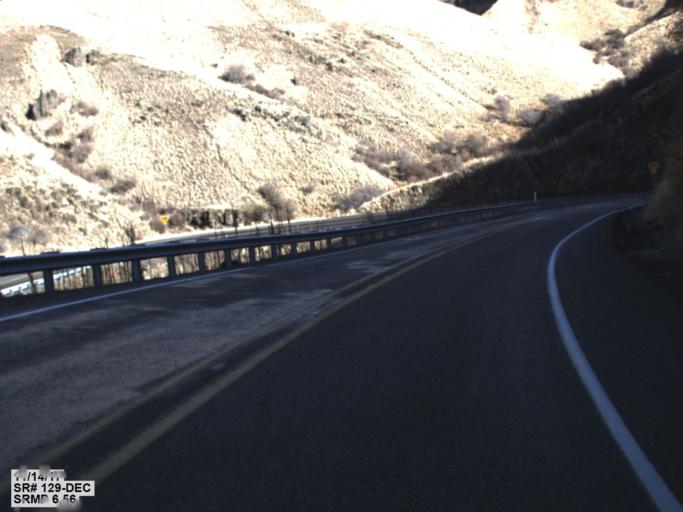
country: US
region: Washington
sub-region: Asotin County
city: Asotin
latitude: 46.0496
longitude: -117.2368
